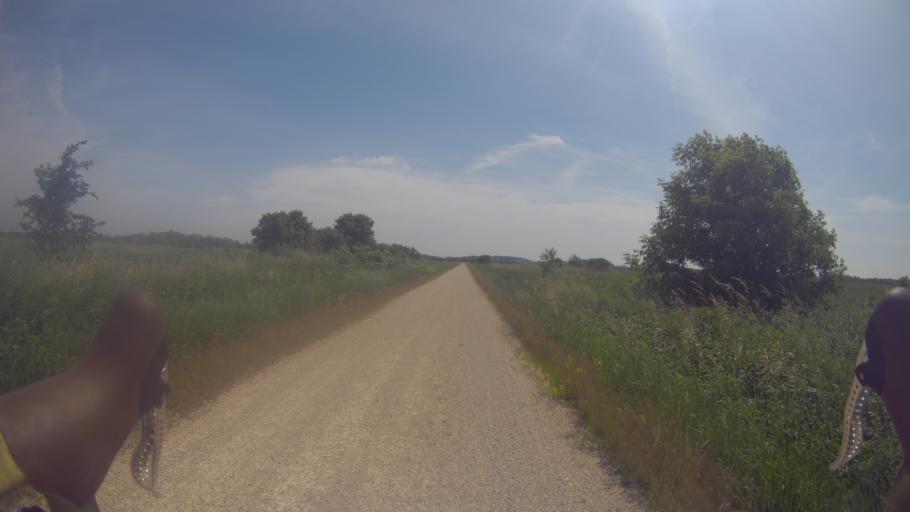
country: US
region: Wisconsin
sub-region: Jefferson County
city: Lake Ripley
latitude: 43.0561
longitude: -88.9852
